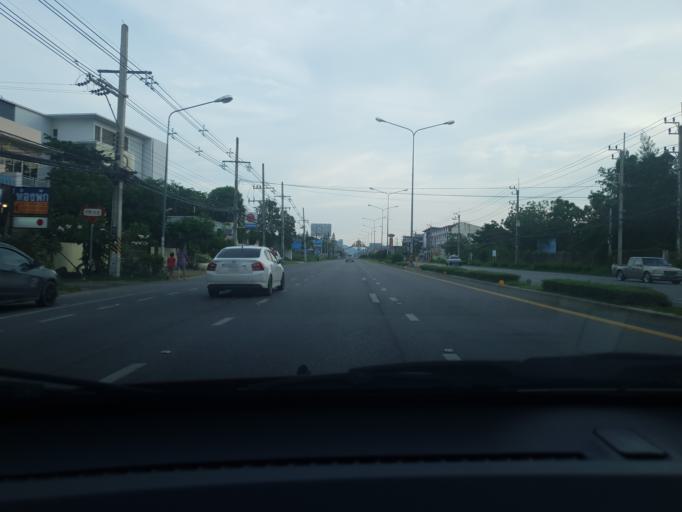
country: TH
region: Prachuap Khiri Khan
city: Hua Hin
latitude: 12.6262
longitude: 99.9509
